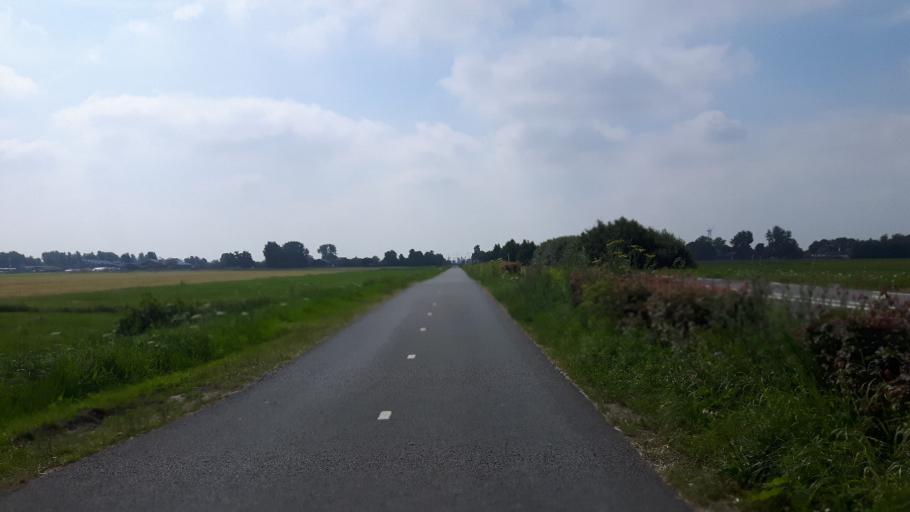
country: NL
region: Utrecht
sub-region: Gemeente Montfoort
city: Montfoort
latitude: 52.0116
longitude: 4.9591
